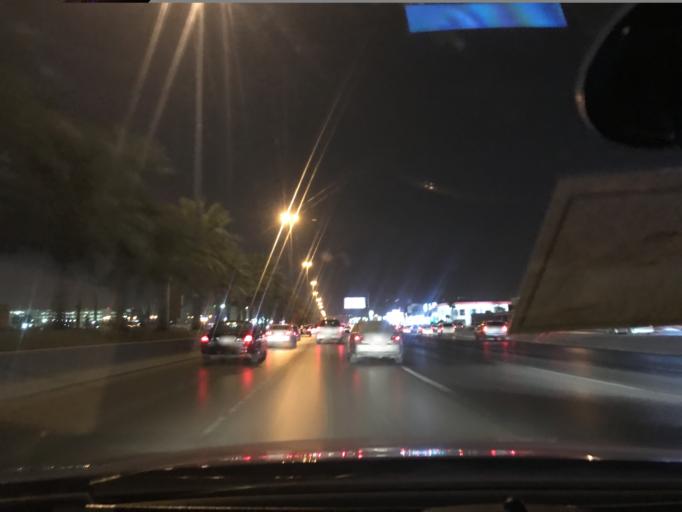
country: SA
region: Ar Riyad
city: Riyadh
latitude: 24.7517
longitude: 46.7430
